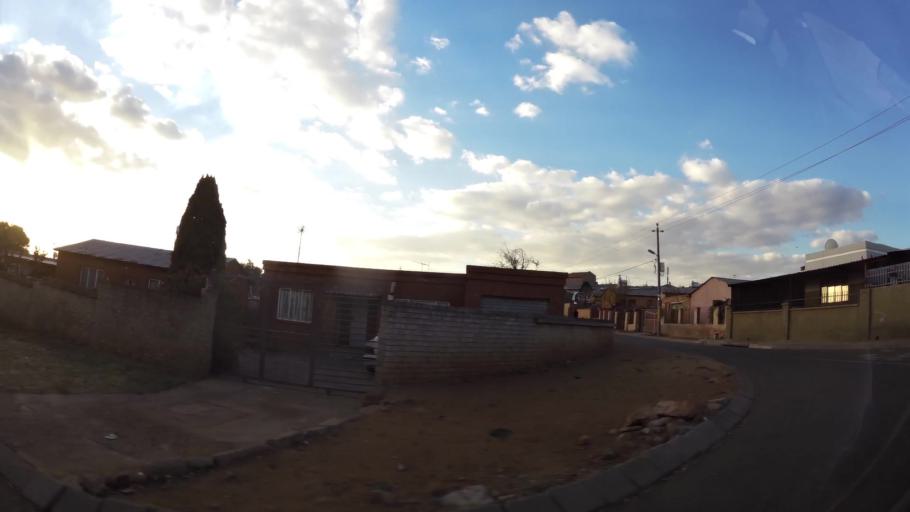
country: ZA
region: Gauteng
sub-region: West Rand District Municipality
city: Krugersdorp
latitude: -26.0769
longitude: 27.7499
